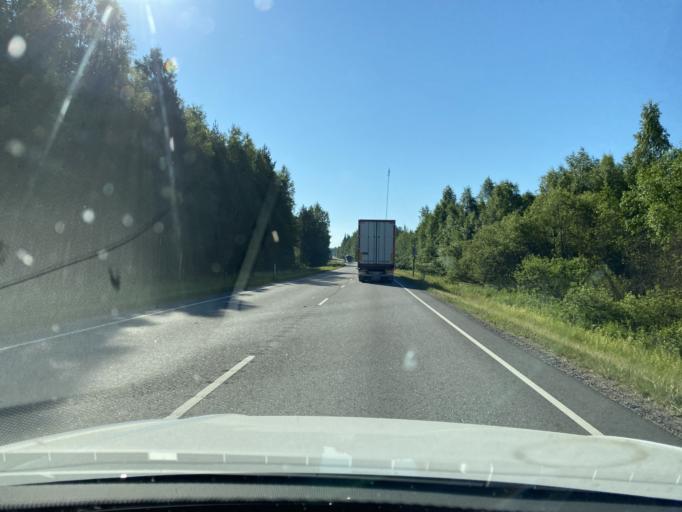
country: FI
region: Haeme
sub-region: Haemeenlinna
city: Renko
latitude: 60.7881
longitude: 24.1317
